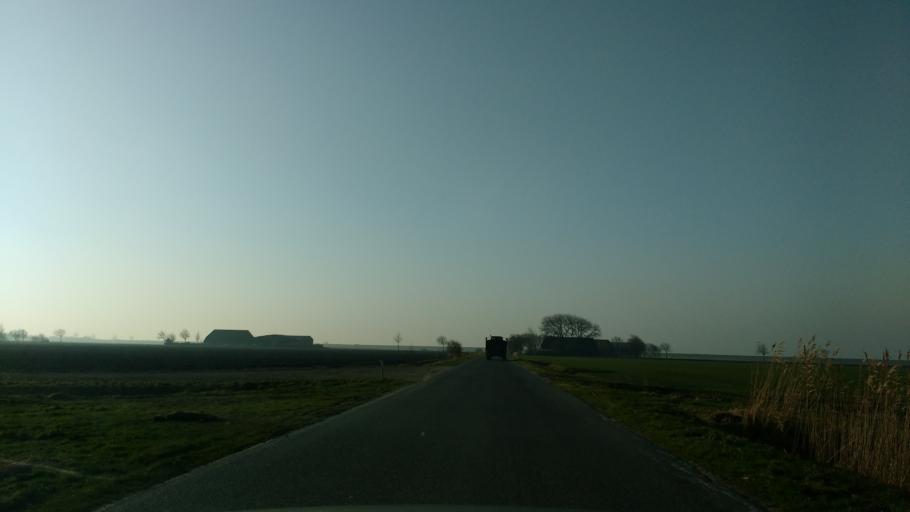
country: DE
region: Schleswig-Holstein
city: Friedrichskoog
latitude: 53.9851
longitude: 8.9204
